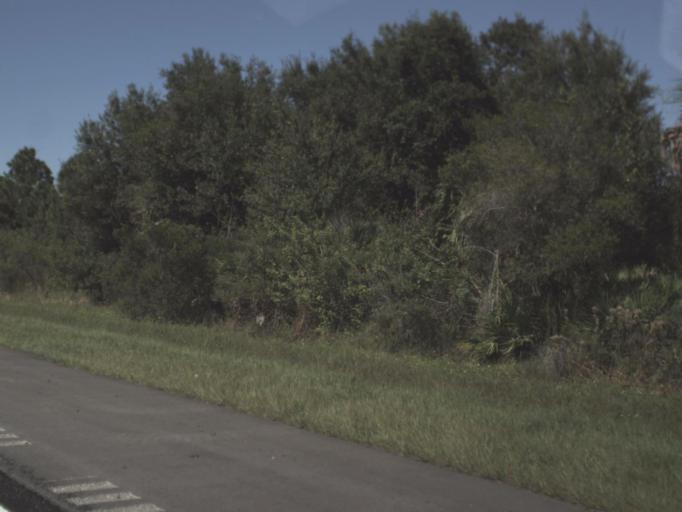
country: US
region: Florida
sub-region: Lee County
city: Suncoast Estates
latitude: 26.7285
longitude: -81.8372
